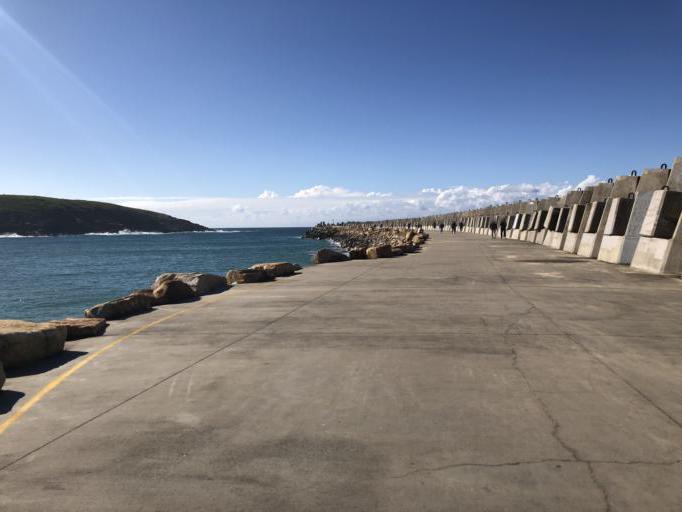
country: AU
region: New South Wales
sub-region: Coffs Harbour
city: Coffs Harbour
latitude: -30.3115
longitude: 153.1504
